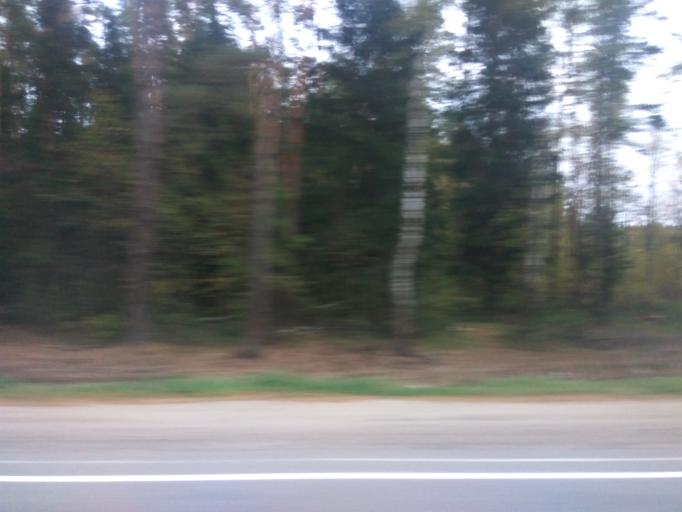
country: RU
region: Moskovskaya
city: Krasnoarmeysk
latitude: 56.0440
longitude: 38.2051
